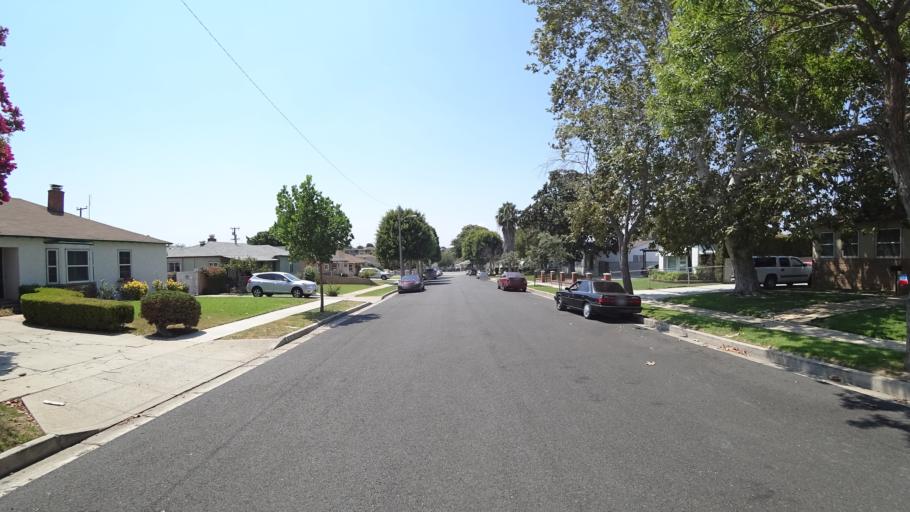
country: US
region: California
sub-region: Los Angeles County
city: Westmont
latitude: 33.9467
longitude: -118.3210
